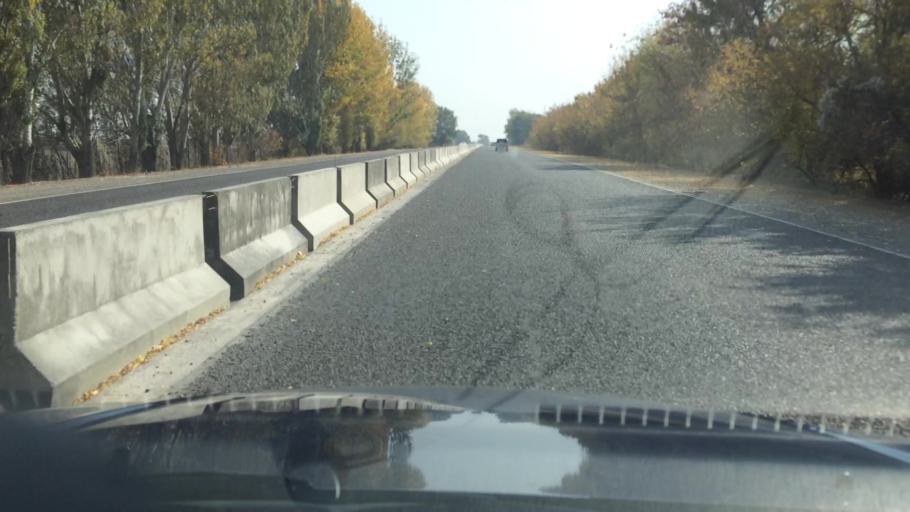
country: KG
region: Chuy
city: Kant
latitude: 42.9638
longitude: 74.9156
